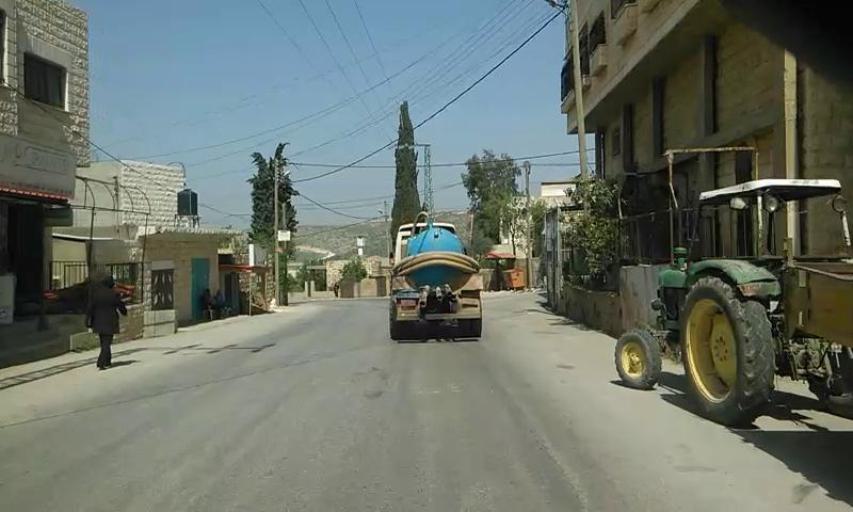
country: PS
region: West Bank
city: Az Zababidah
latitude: 32.3882
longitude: 35.3227
